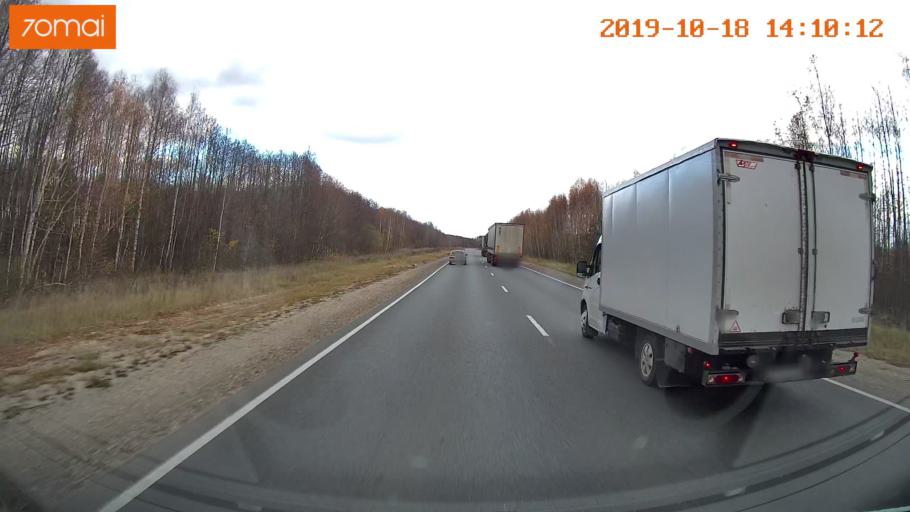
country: RU
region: Rjazan
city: Spas-Klepiki
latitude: 55.1430
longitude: 40.2003
